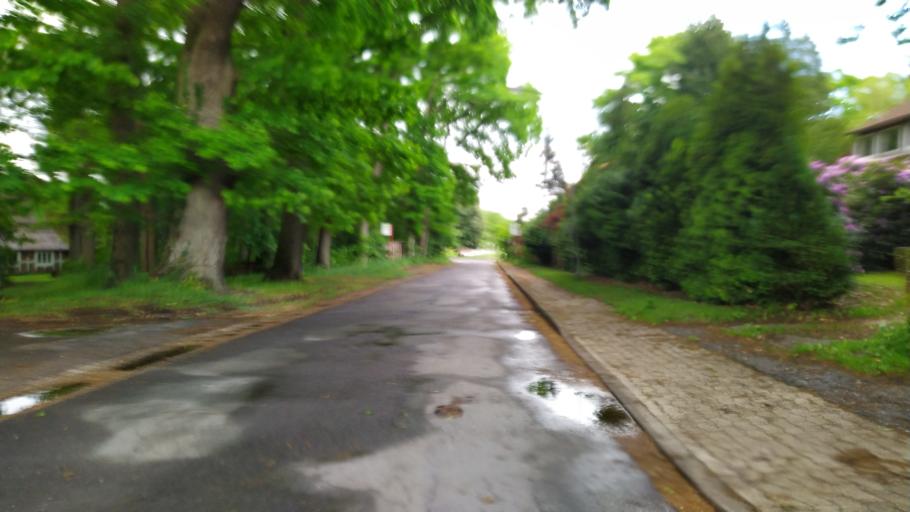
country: DE
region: Lower Saxony
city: Brest
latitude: 53.4319
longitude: 9.3558
